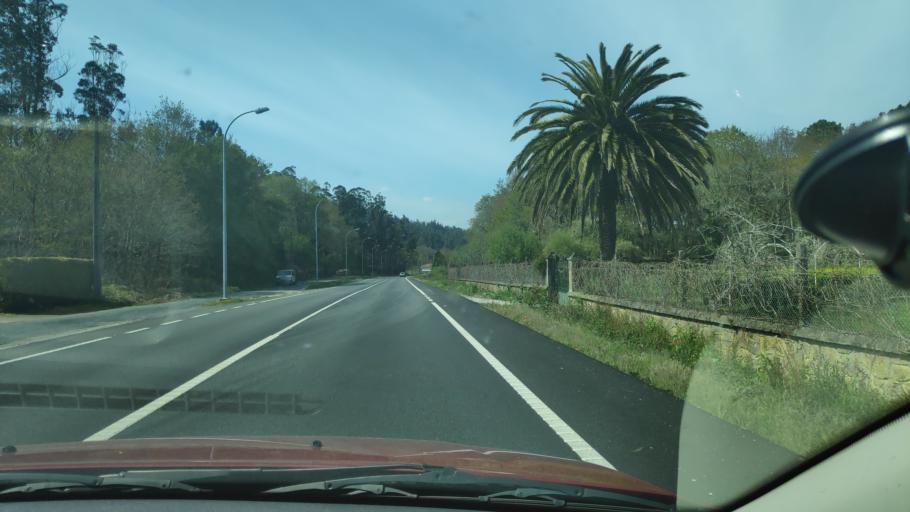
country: ES
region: Galicia
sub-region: Provincia da Coruna
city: Ames
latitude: 42.8807
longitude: -8.6789
